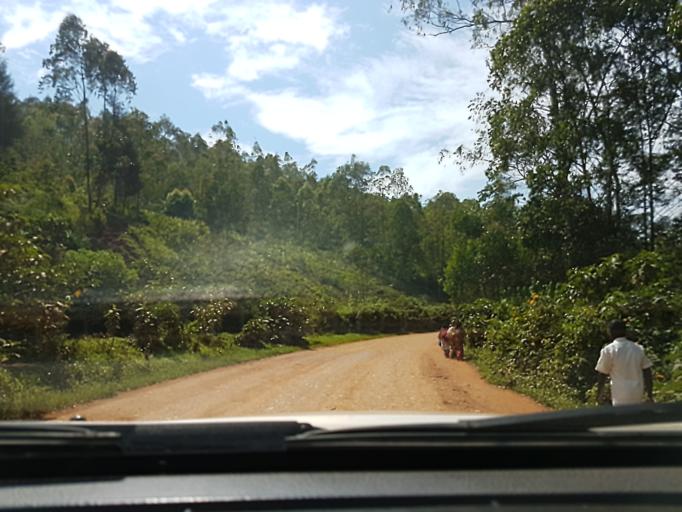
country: CD
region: South Kivu
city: Bukavu
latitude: -2.6473
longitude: 28.8735
